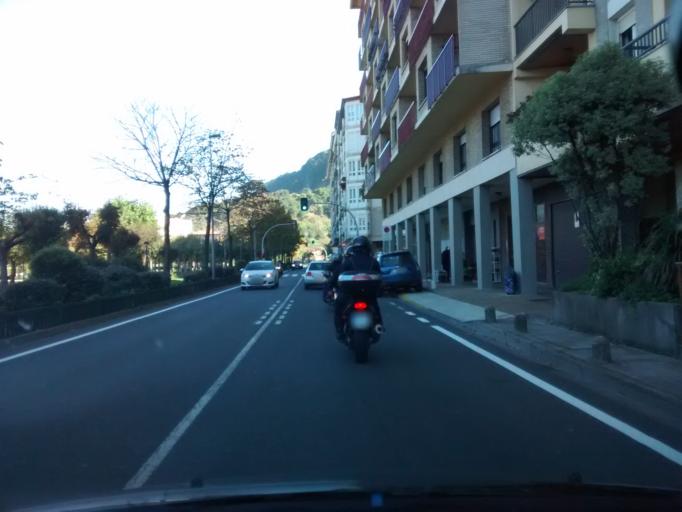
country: ES
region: Basque Country
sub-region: Provincia de Guipuzcoa
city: Deba
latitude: 43.2953
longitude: -2.3545
